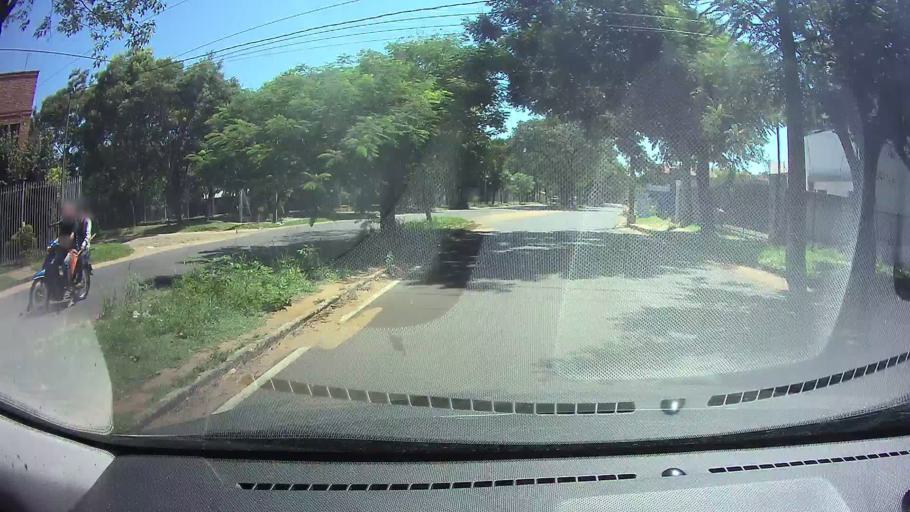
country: PY
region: Central
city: Fernando de la Mora
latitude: -25.2918
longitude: -57.5219
